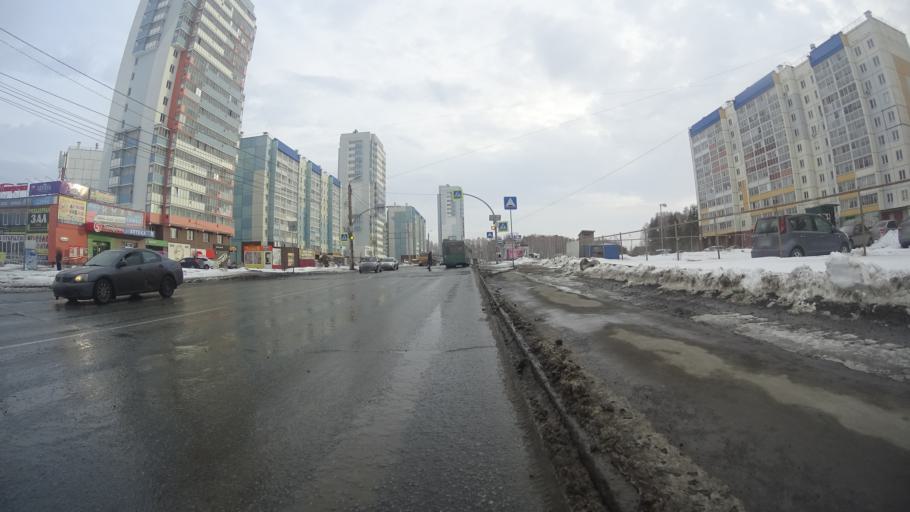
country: RU
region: Chelyabinsk
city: Roshchino
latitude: 55.2043
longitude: 61.2843
